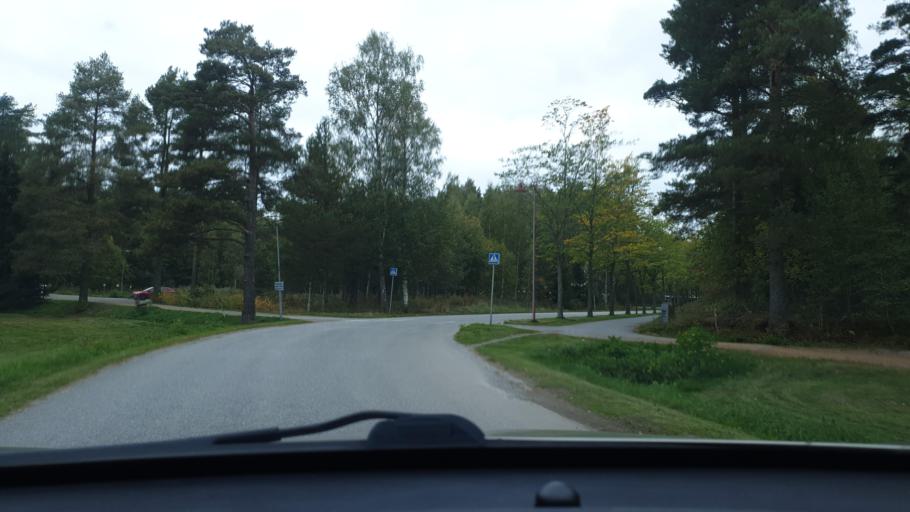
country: FI
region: Ostrobothnia
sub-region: Vaasa
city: Teeriniemi
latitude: 63.0884
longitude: 21.6744
